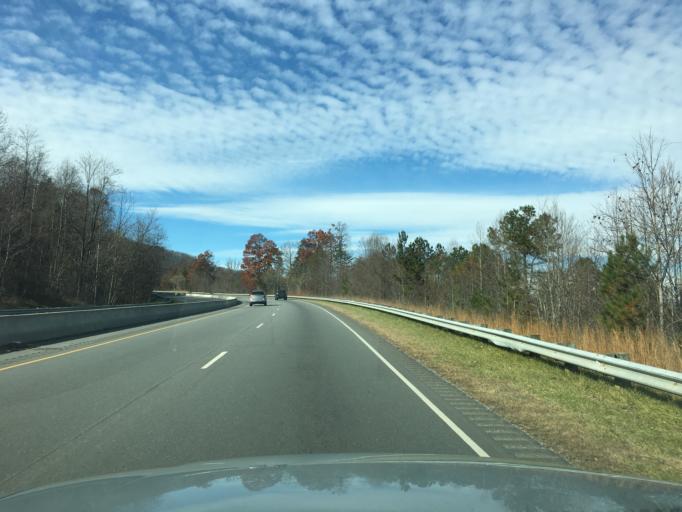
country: US
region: North Carolina
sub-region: McDowell County
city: Marion
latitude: 35.6685
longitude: -81.9900
